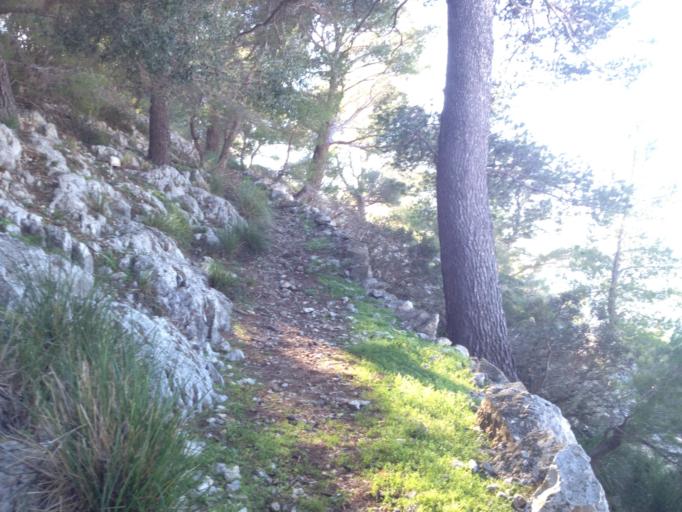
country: ES
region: Balearic Islands
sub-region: Illes Balears
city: Pollenca
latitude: 39.8692
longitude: 3.0211
